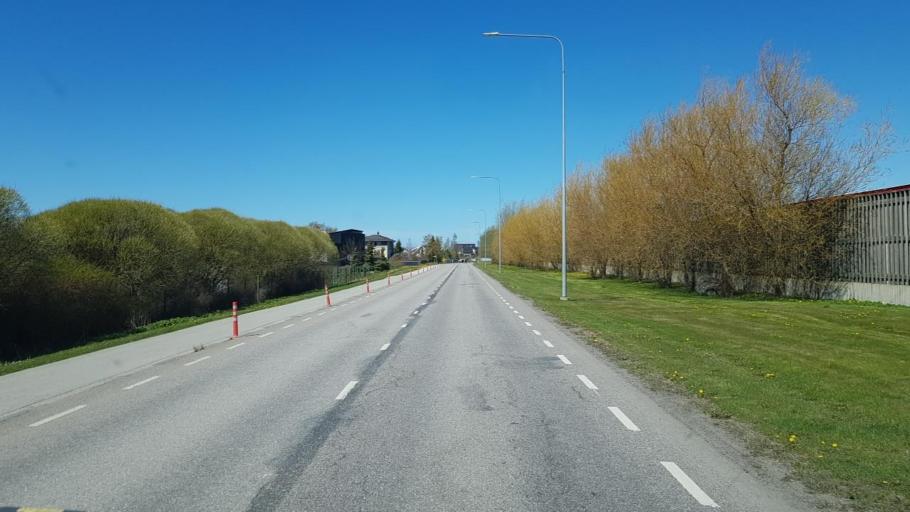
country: EE
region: Harju
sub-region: Viimsi vald
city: Haabneeme
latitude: 59.5022
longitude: 24.8181
